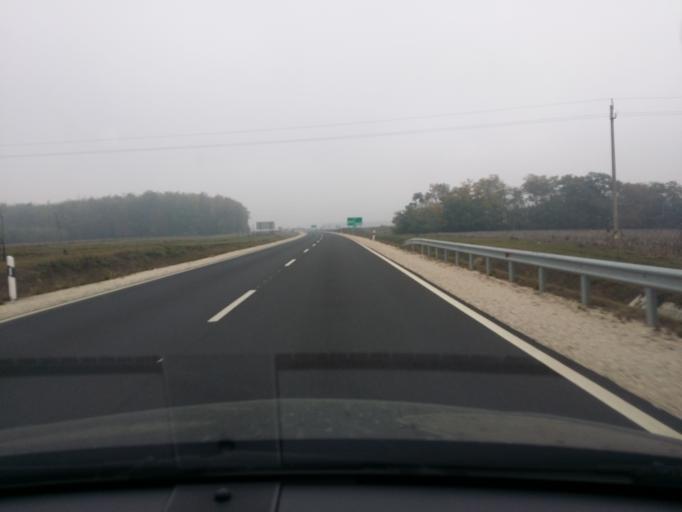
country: HU
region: Szabolcs-Szatmar-Bereg
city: Nyiregyhaza
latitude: 47.9405
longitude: 21.6499
